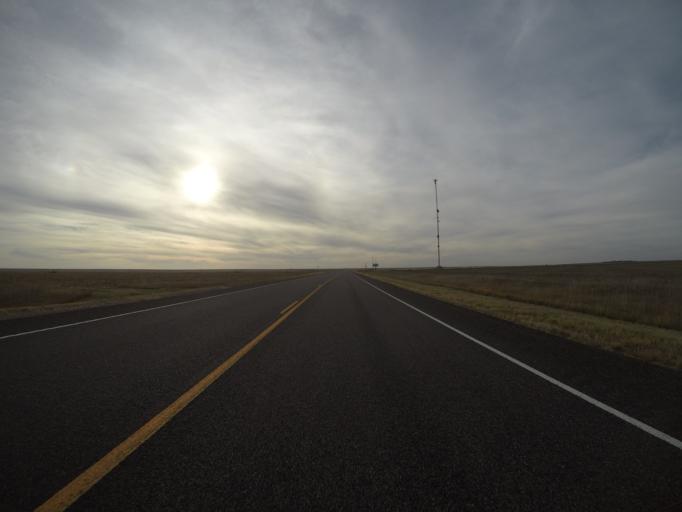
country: US
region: Kansas
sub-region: Cheyenne County
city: Saint Francis
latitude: 39.7470
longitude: -102.0610
